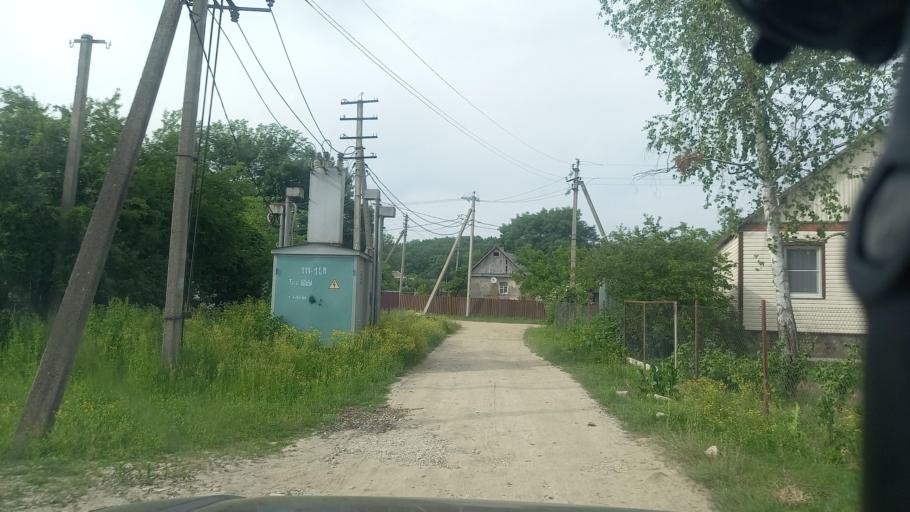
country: RU
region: Krasnodarskiy
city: Goryachiy Klyuch
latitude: 44.6066
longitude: 39.0244
